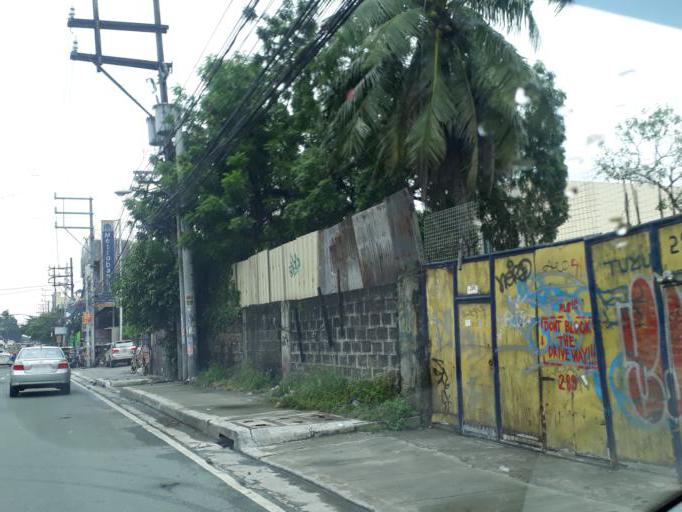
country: PH
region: Calabarzon
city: Del Monte
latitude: 14.6522
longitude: 121.0182
